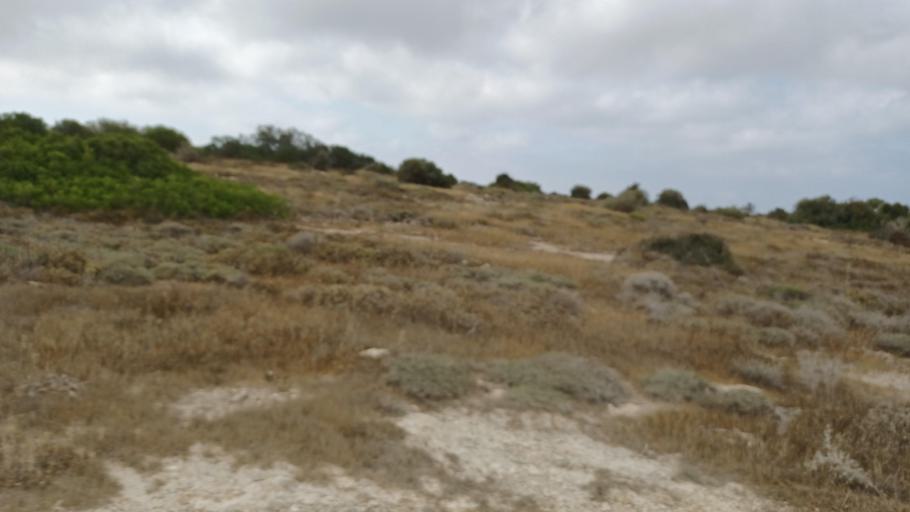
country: CY
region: Ammochostos
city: Protaras
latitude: 35.0020
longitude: 34.0293
